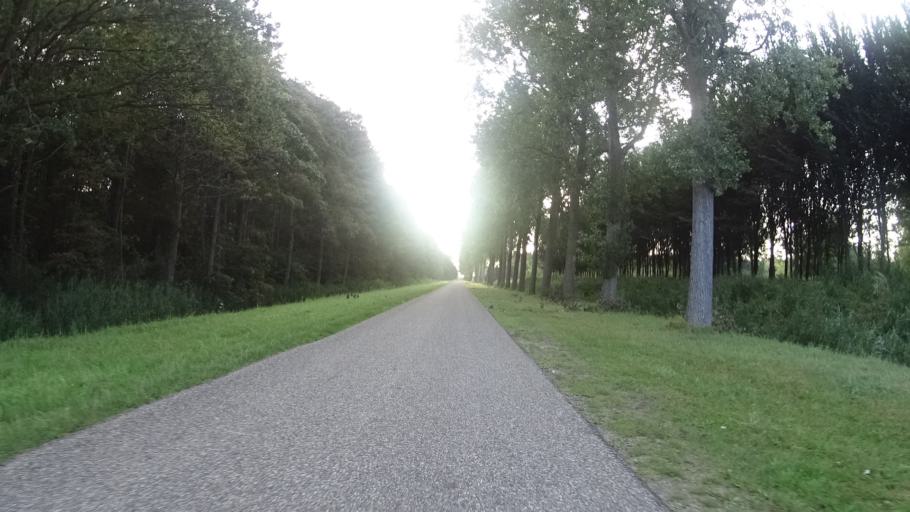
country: NL
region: North Holland
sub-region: Gemeente Hollands Kroon
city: Den Oever
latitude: 52.9029
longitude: 5.0464
